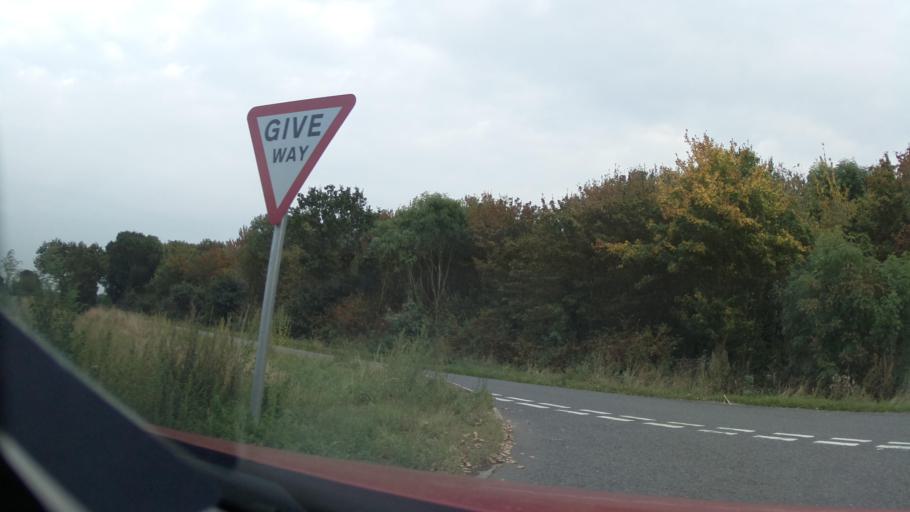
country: GB
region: England
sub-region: Nottinghamshire
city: South Collingham
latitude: 53.1430
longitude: -0.6681
